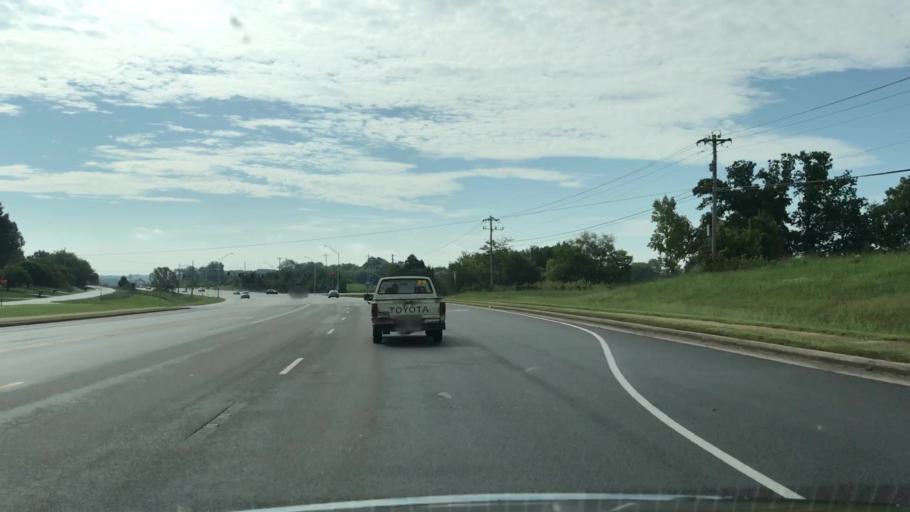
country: US
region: Kentucky
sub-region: Warren County
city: Plano
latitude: 36.9064
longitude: -86.4006
